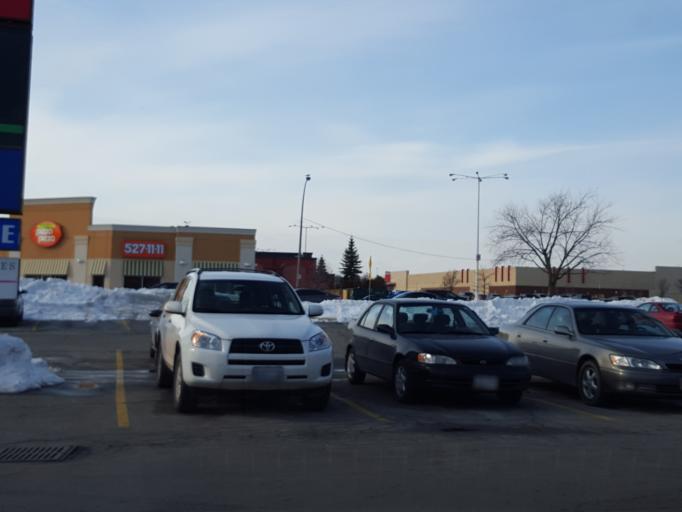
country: CA
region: Ontario
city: Burlington
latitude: 43.3450
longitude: -79.7938
